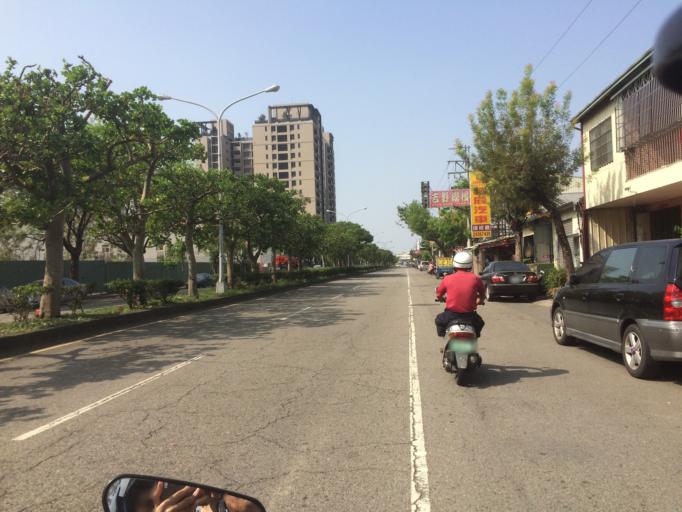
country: TW
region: Taiwan
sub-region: Taichung City
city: Taichung
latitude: 24.1824
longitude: 120.7172
